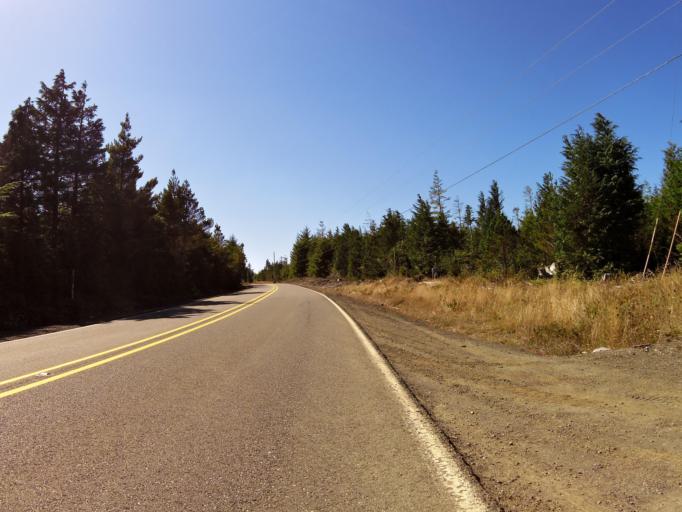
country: US
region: Oregon
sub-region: Coos County
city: Barview
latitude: 43.2778
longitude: -124.3523
